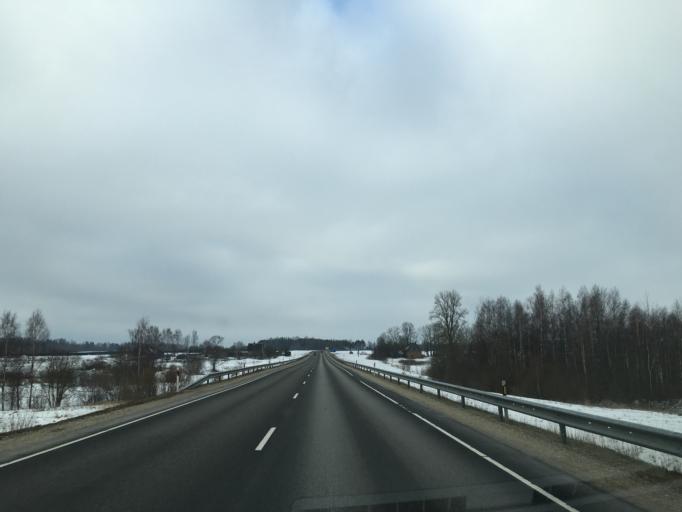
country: EE
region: Tartu
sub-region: Elva linn
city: Elva
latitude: 58.1948
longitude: 26.3520
